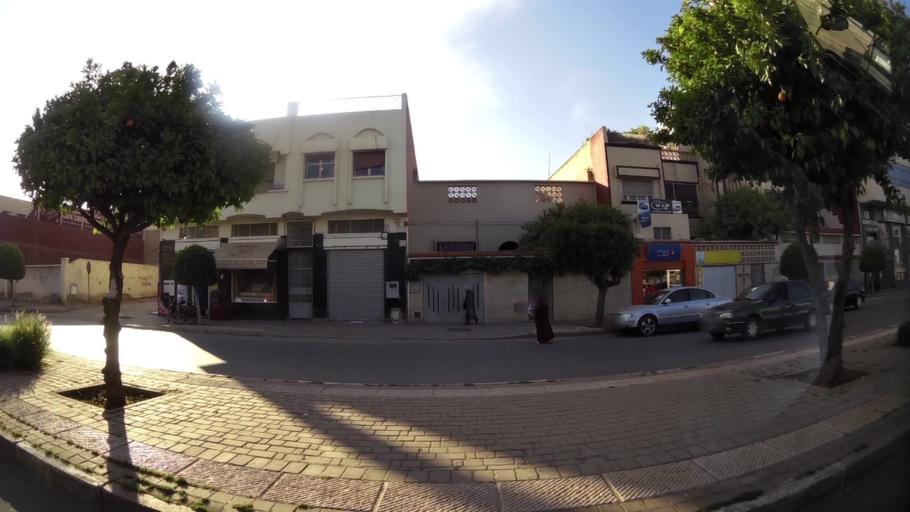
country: MA
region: Oriental
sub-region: Oujda-Angad
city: Oujda
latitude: 34.6955
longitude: -1.9032
